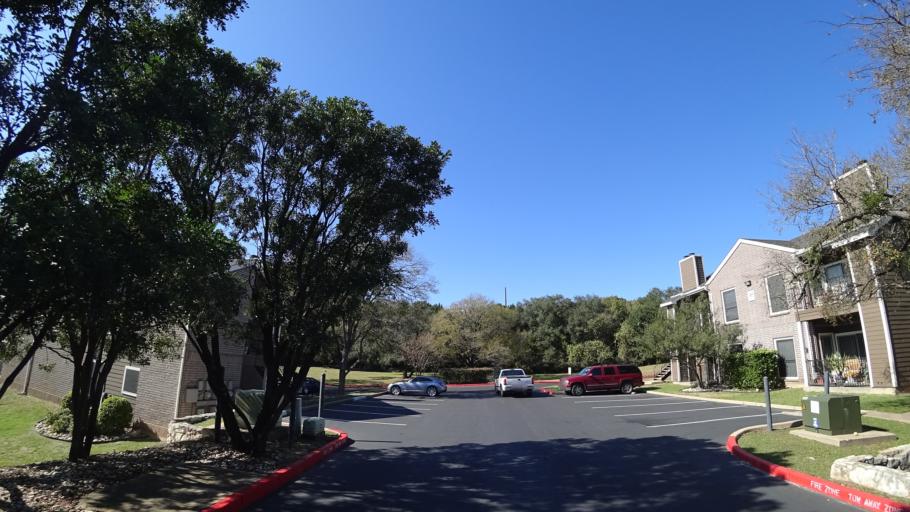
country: US
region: Texas
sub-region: Williamson County
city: Jollyville
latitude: 30.4112
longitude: -97.7508
